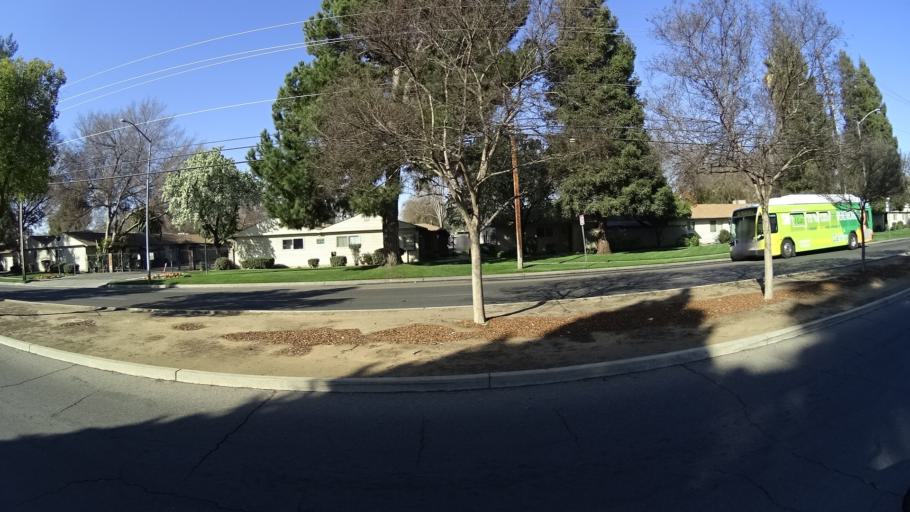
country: US
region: California
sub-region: Fresno County
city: Fresno
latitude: 36.7278
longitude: -119.7364
